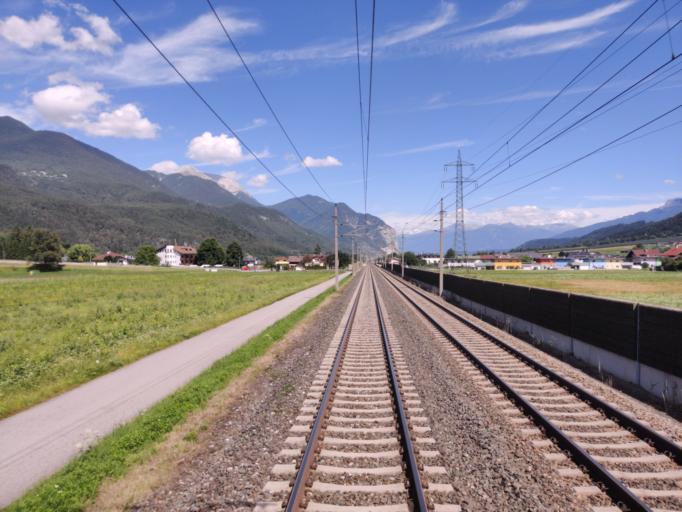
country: AT
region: Tyrol
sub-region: Politischer Bezirk Innsbruck Land
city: Hatting
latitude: 47.2816
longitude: 11.1666
